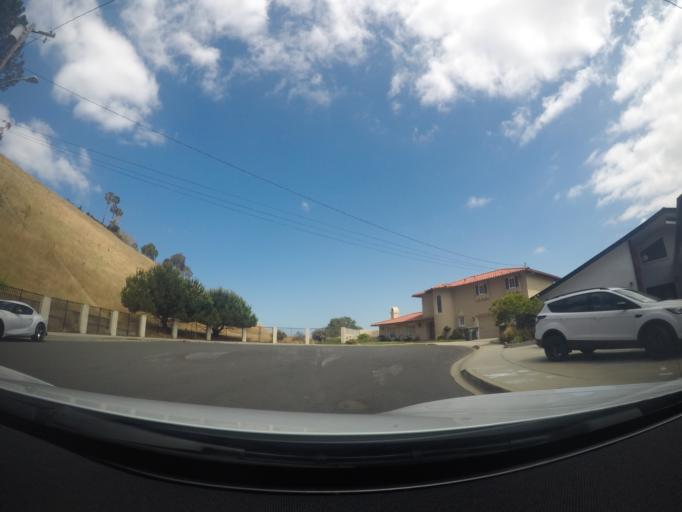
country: US
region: California
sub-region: Los Angeles County
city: Rolling Hills Estates
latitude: 33.8067
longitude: -118.3646
